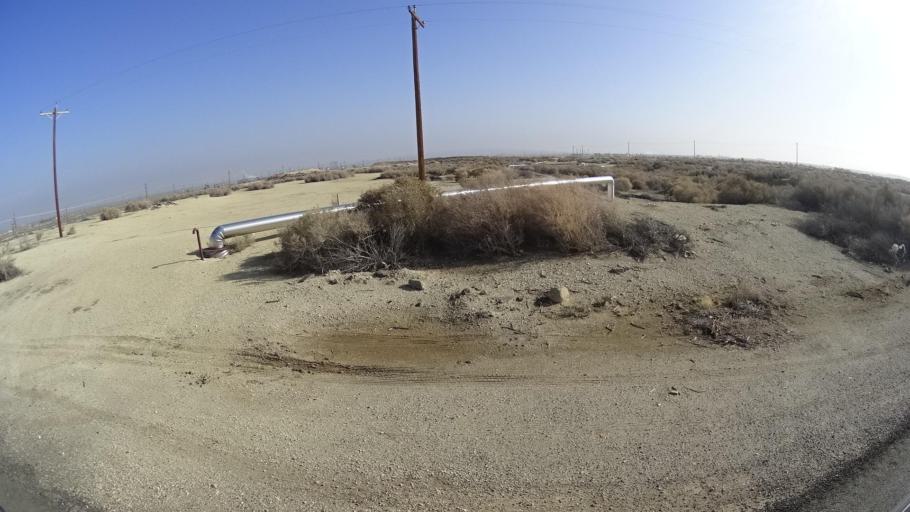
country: US
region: California
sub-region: Kern County
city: Taft Heights
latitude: 35.2074
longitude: -119.5696
